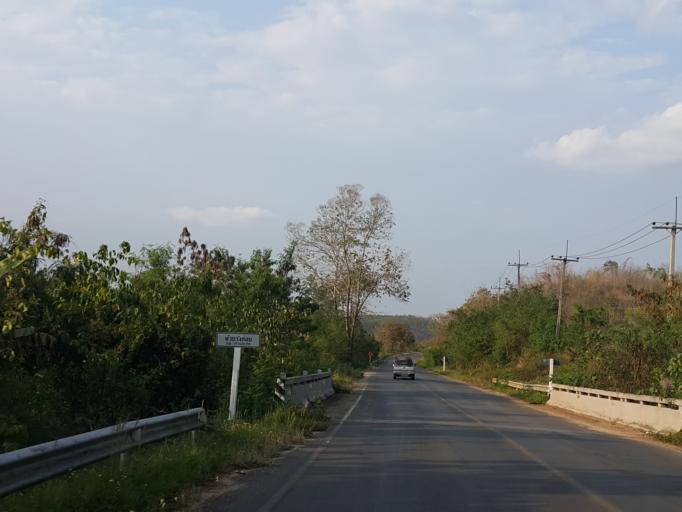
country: TH
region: Lampang
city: Lampang
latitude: 18.4560
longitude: 99.4578
